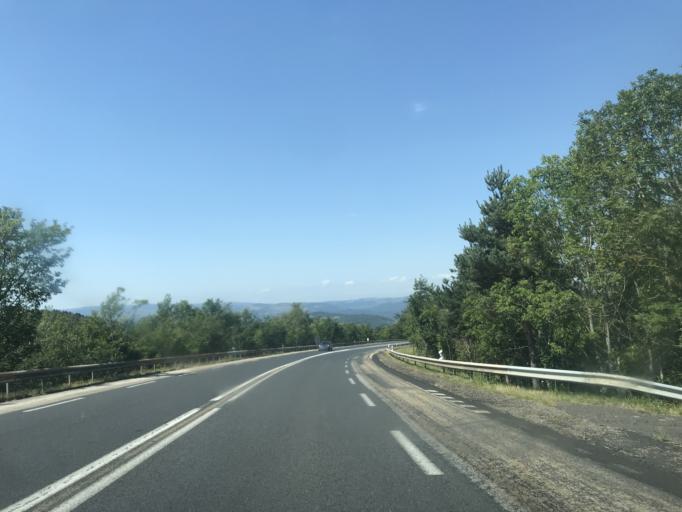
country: FR
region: Auvergne
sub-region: Departement de la Haute-Loire
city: Paulhaguet
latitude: 45.1370
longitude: 3.6054
